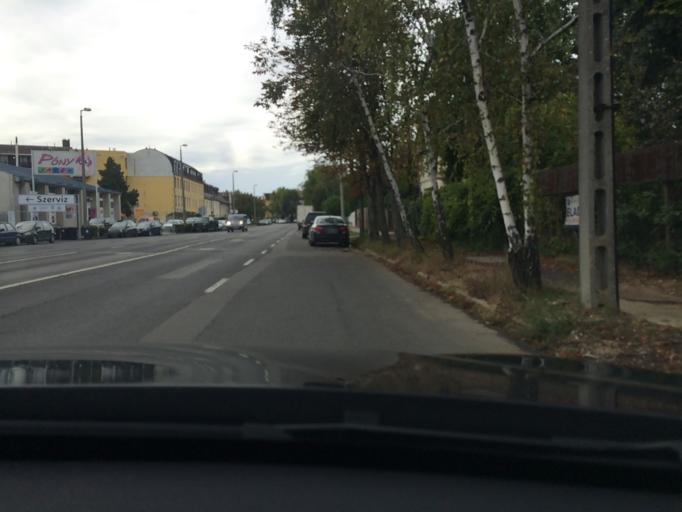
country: HU
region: Szabolcs-Szatmar-Bereg
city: Nyiregyhaza
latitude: 47.9627
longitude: 21.7242
